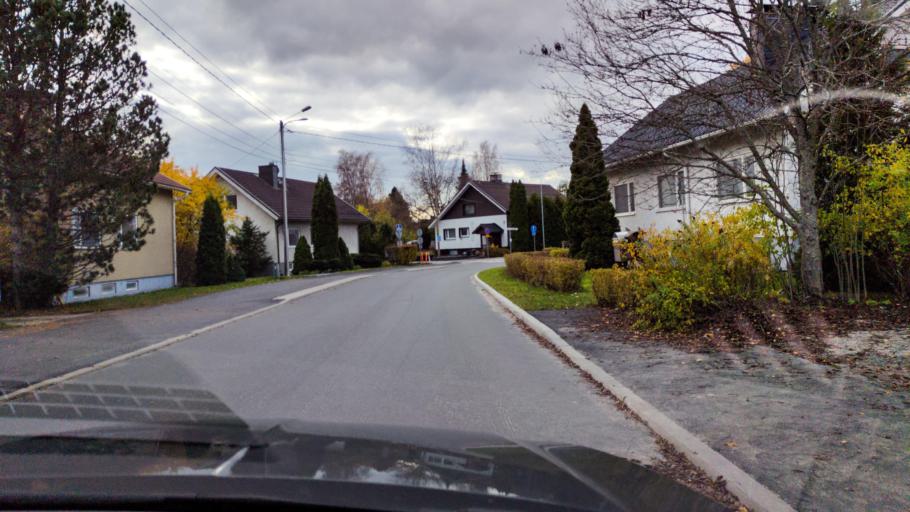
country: FI
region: Varsinais-Suomi
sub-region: Turku
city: Turku
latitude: 60.4667
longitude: 22.2545
